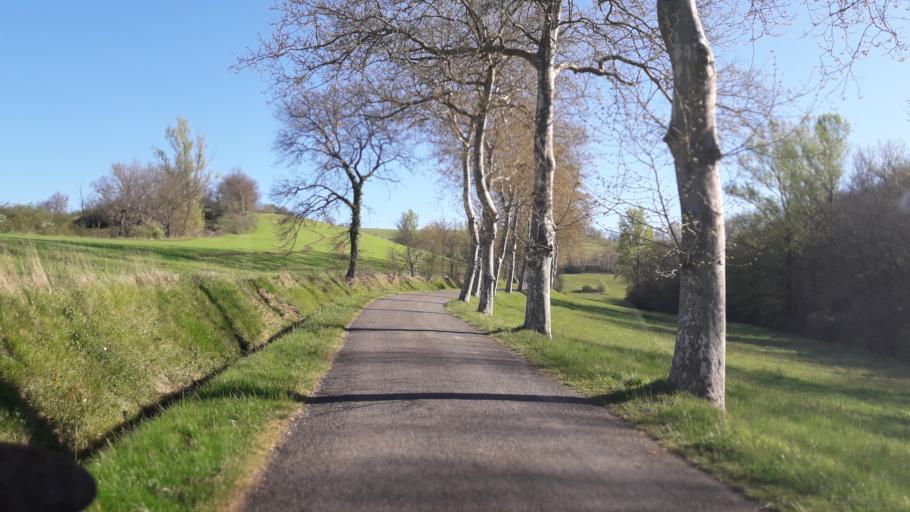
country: FR
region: Midi-Pyrenees
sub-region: Departement de la Haute-Garonne
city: Montesquieu-Volvestre
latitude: 43.1993
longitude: 1.2680
